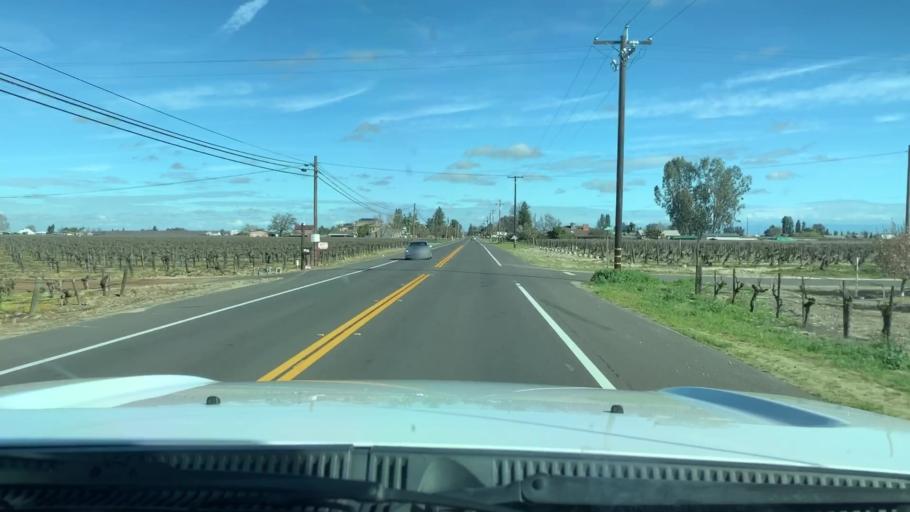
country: US
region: California
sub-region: Fresno County
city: Selma
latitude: 36.5542
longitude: -119.6826
